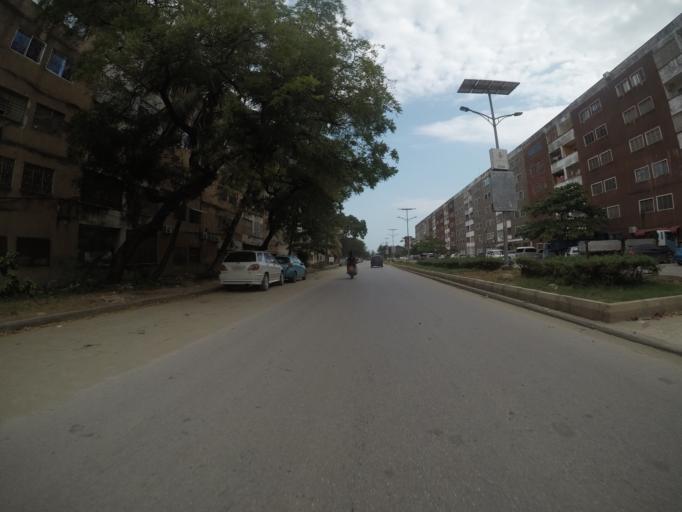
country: TZ
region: Zanzibar Urban/West
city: Zanzibar
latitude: -6.1688
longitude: 39.1988
